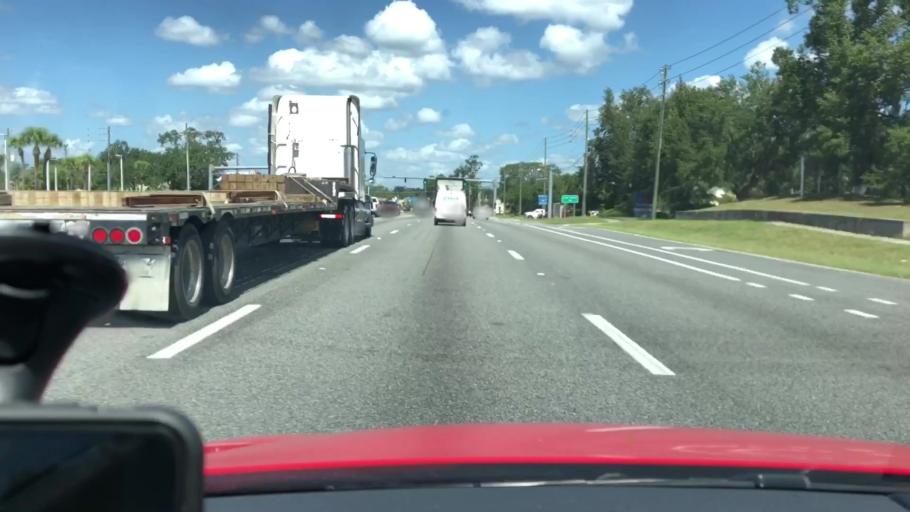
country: US
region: Florida
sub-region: Volusia County
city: De Land Southwest
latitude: 28.9831
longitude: -81.2993
